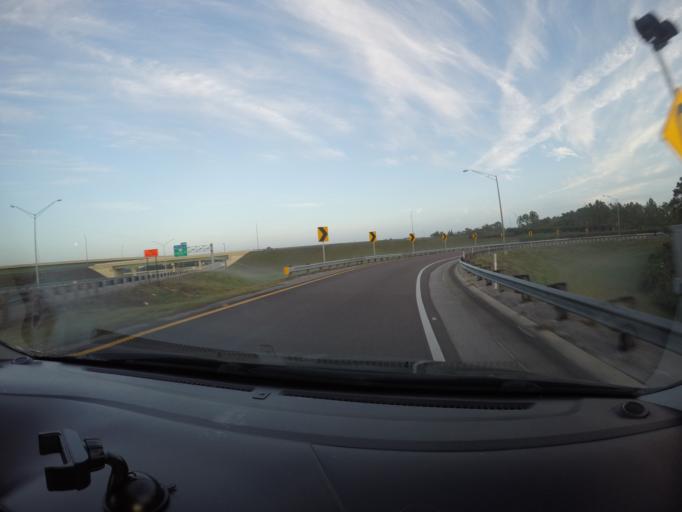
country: US
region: Florida
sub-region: Orange County
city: Union Park
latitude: 28.5484
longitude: -81.2586
